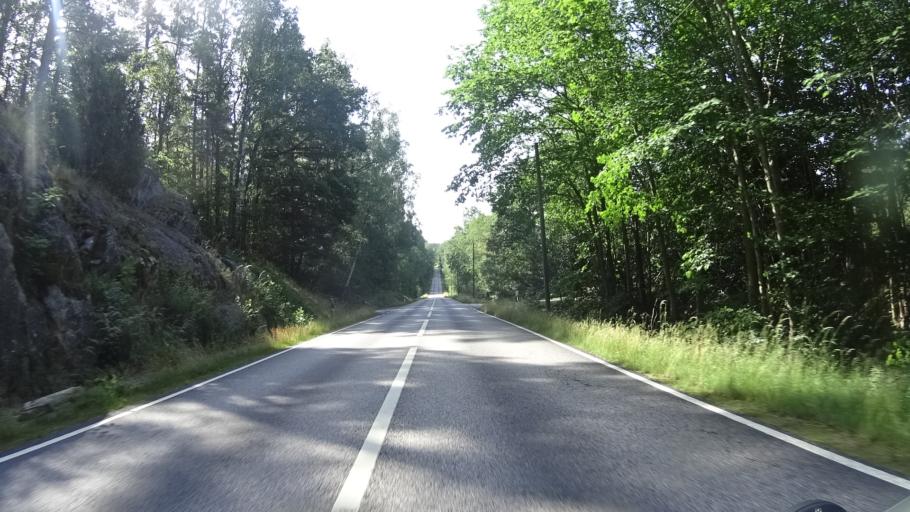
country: SE
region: Kalmar
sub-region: Vasterviks Kommun
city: Overum
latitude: 58.0382
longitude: 16.2268
